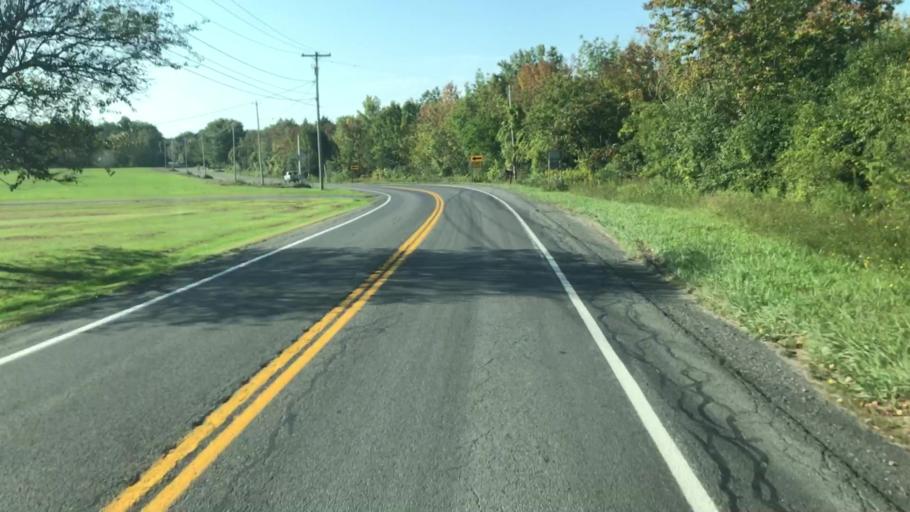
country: US
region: New York
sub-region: Onondaga County
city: Skaneateles
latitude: 42.9918
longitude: -76.4287
